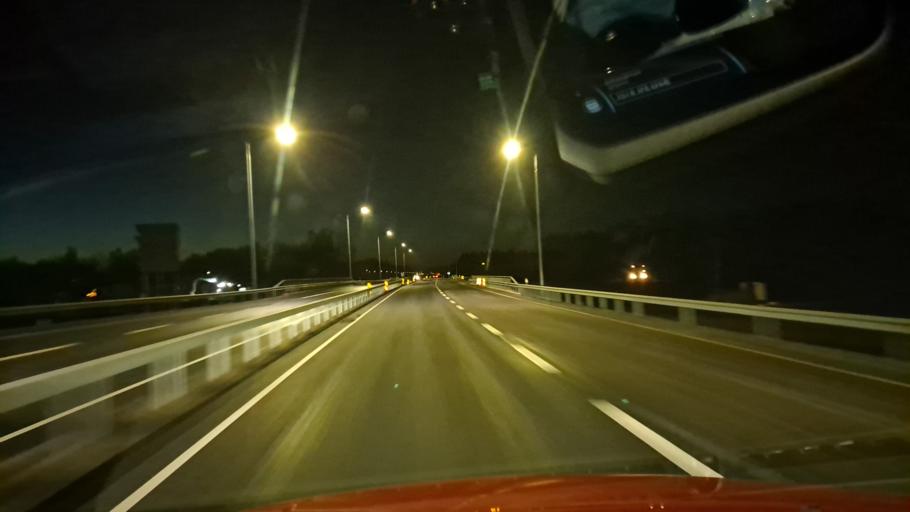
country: FI
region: Lapland
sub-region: Kemi-Tornio
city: Simo
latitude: 65.6694
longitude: 24.9293
